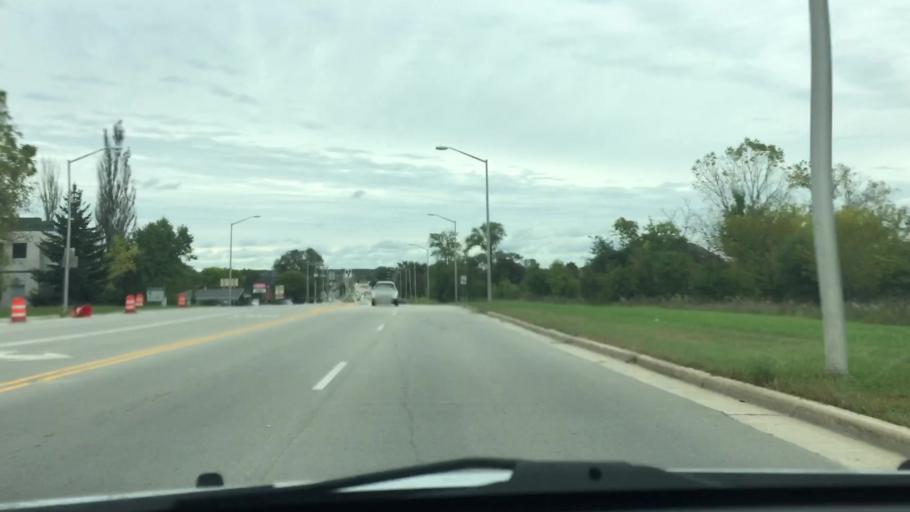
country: US
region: Wisconsin
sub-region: Waukesha County
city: Waukesha
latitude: 43.0327
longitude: -88.2559
